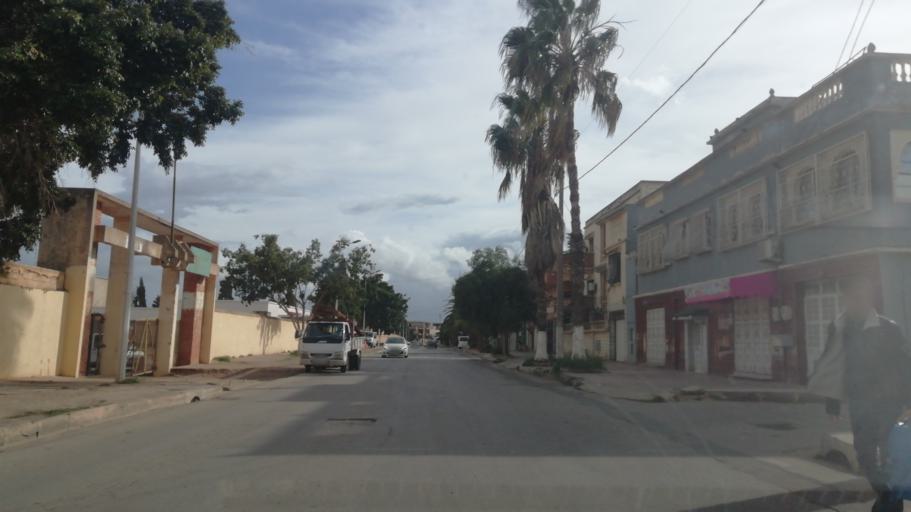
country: DZ
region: Oran
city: Es Senia
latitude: 35.6648
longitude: -0.6400
